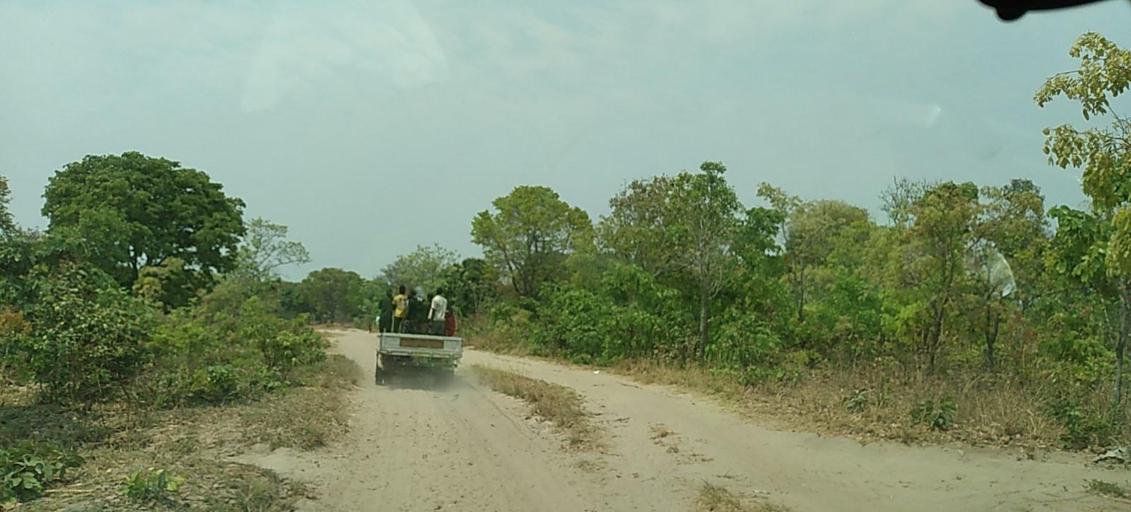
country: ZM
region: North-Western
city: Kabompo
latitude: -13.4878
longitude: 24.4615
